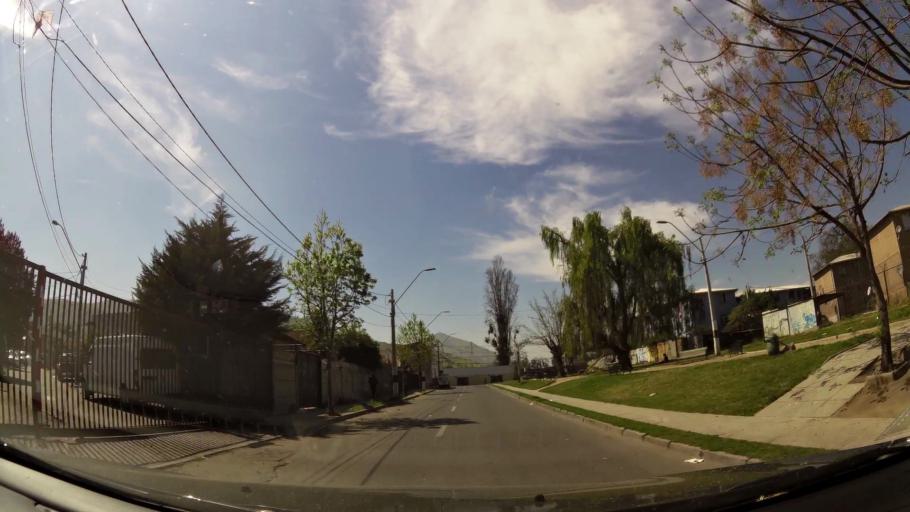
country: CL
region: Santiago Metropolitan
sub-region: Provincia de Santiago
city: Lo Prado
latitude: -33.4022
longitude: -70.7468
